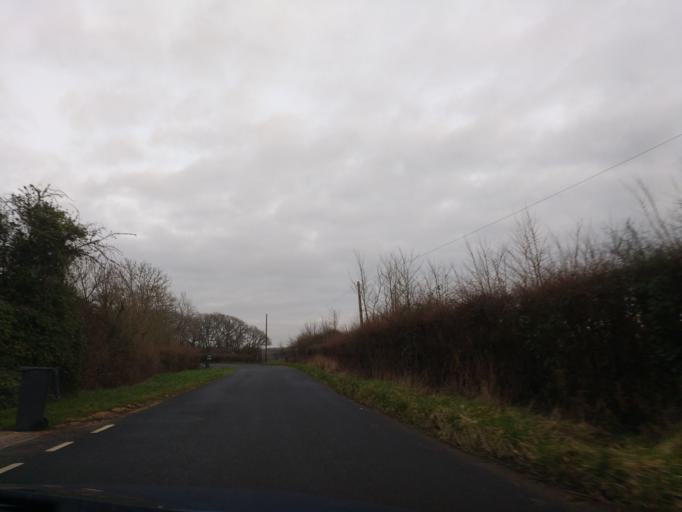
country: GB
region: England
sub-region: Isle of Wight
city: Shalfleet
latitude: 50.7159
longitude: -1.3720
